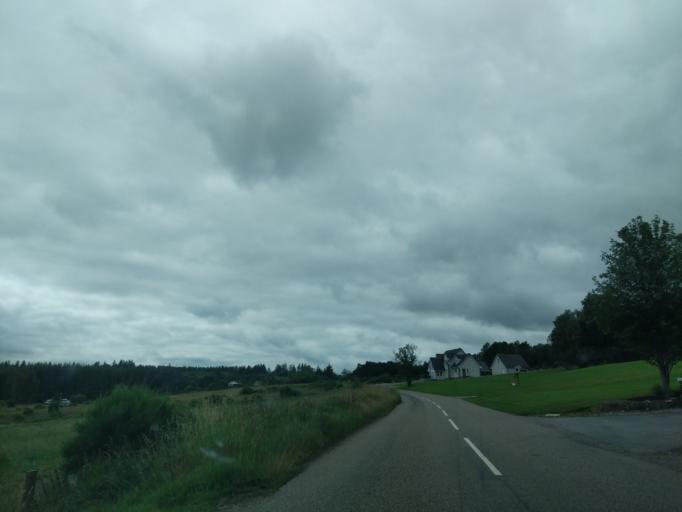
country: GB
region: Scotland
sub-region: Moray
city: Rothes
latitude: 57.4862
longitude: -3.2505
